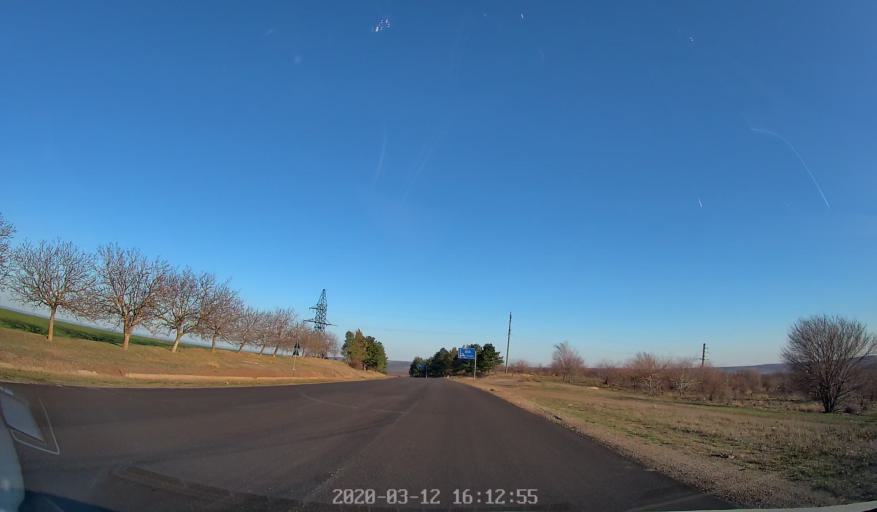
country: MD
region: Anenii Noi
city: Anenii Noi
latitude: 46.9299
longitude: 29.2799
